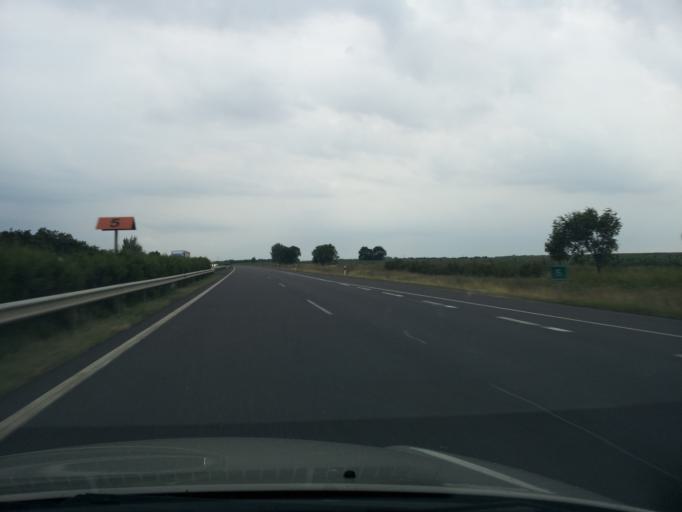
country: HU
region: Borsod-Abauj-Zemplen
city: Emod
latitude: 47.9152
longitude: 20.8427
